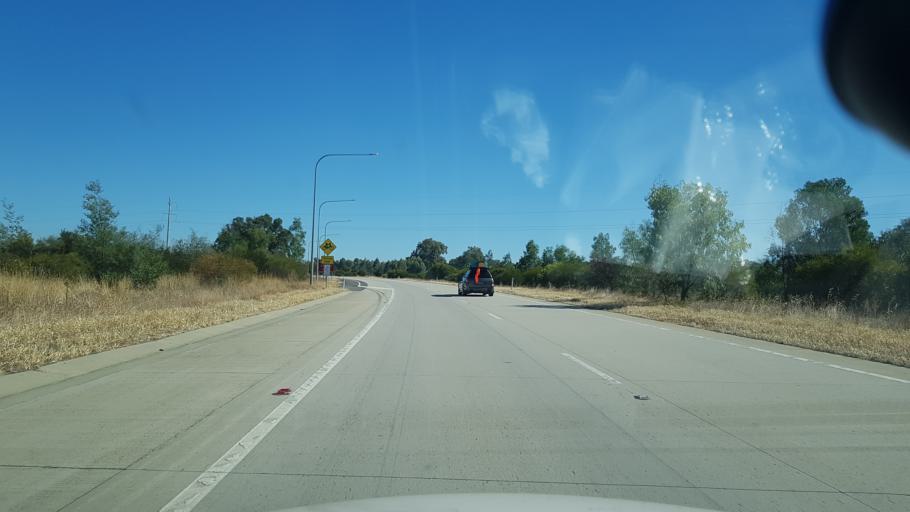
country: AU
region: New South Wales
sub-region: Greater Hume Shire
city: Jindera
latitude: -35.9269
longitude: 147.0070
